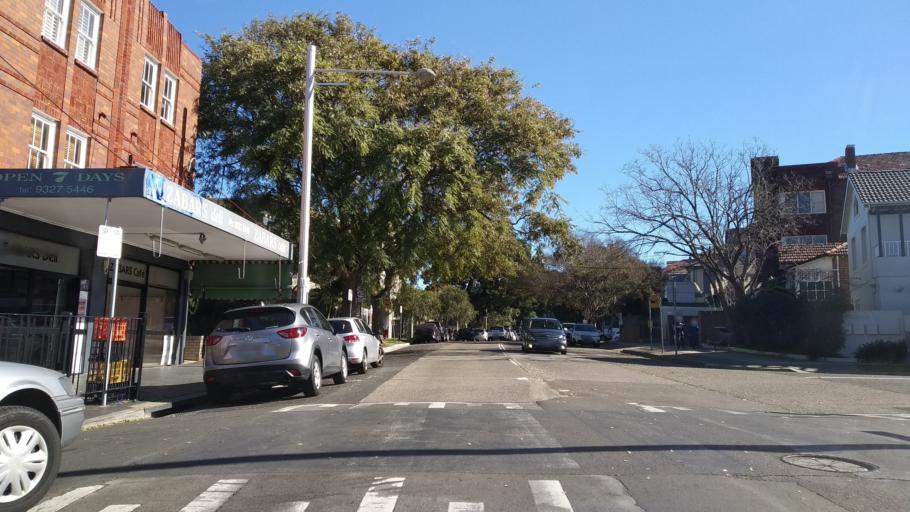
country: AU
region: New South Wales
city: Edgecliff
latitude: -33.8861
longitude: 151.2571
